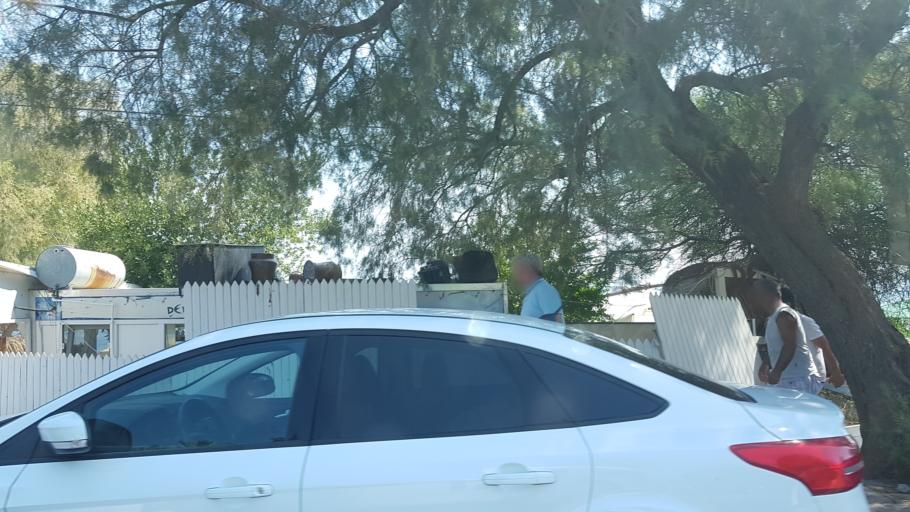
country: TR
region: Izmir
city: Urla
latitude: 38.3722
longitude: 26.7620
